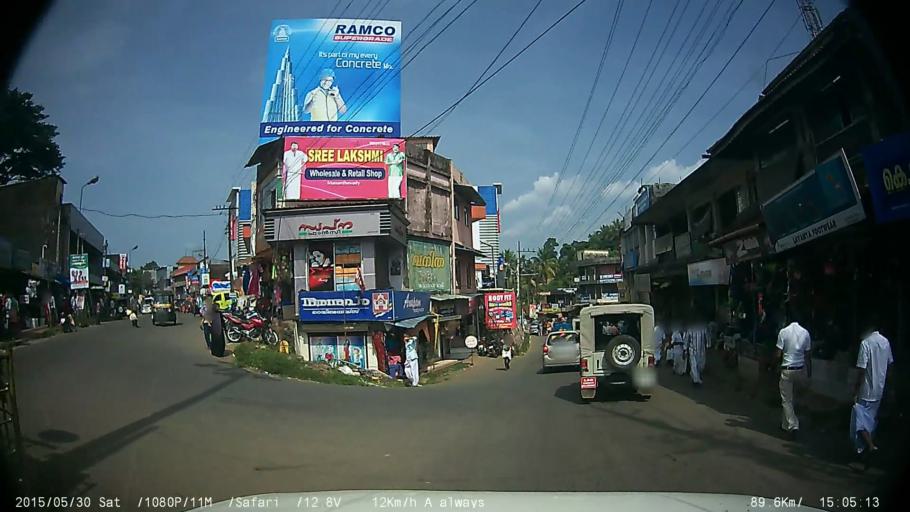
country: IN
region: Kerala
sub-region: Wayanad
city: Panamaram
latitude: 11.8034
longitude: 76.0053
